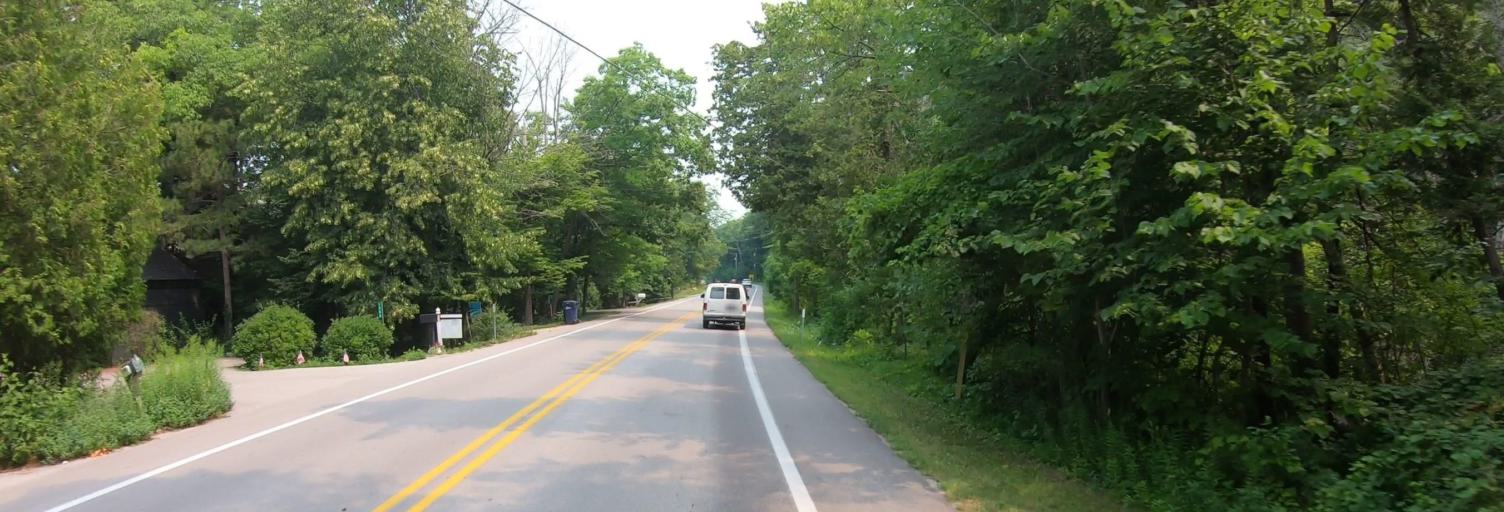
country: US
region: Michigan
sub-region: Leelanau County
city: Leland
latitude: 44.9578
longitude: -85.7974
